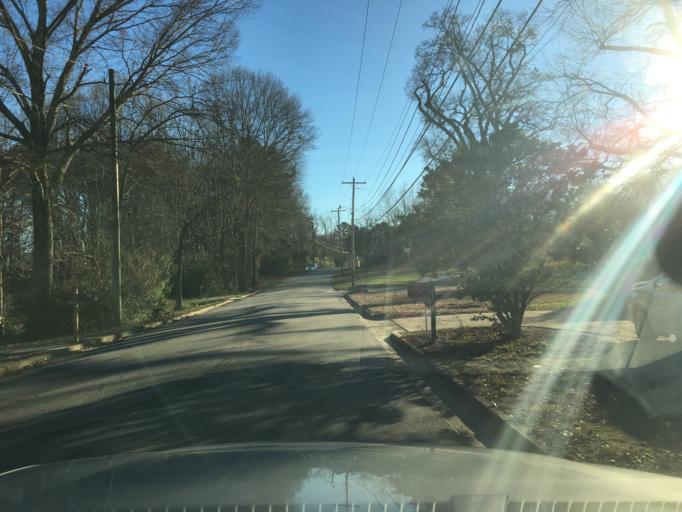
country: US
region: South Carolina
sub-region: Greenville County
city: Greer
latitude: 34.9410
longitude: -82.2433
